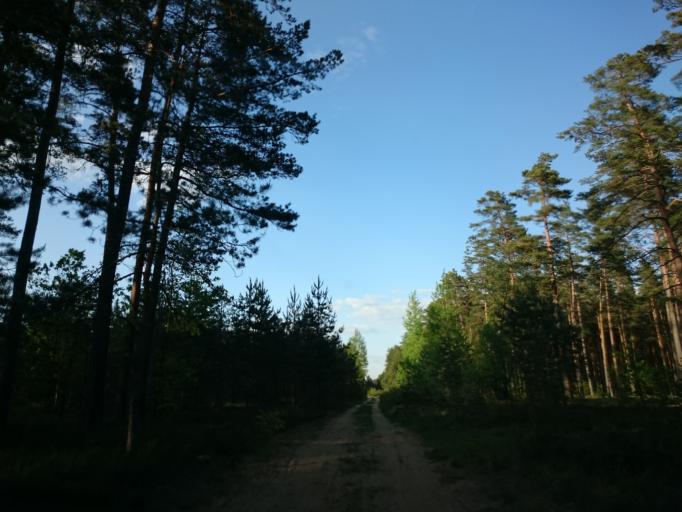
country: LV
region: Stopini
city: Ulbroka
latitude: 56.9517
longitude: 24.2904
